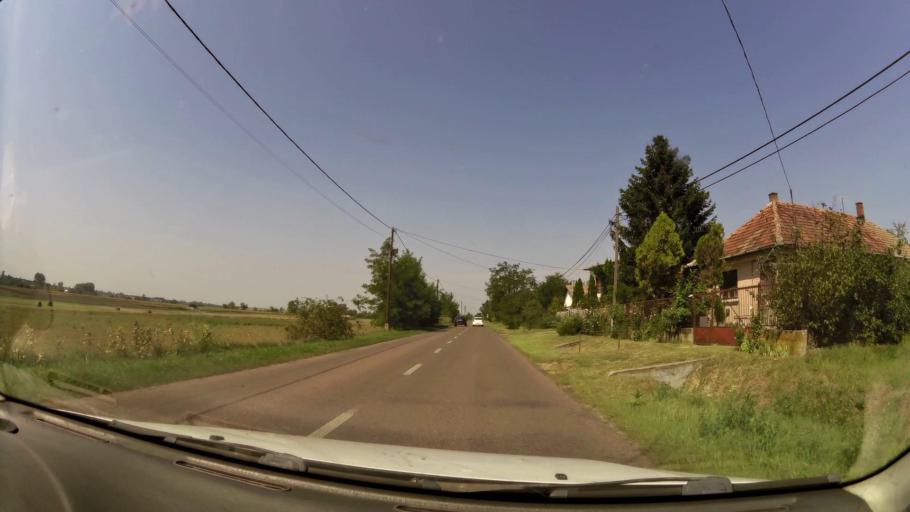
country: HU
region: Pest
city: Tapiobicske
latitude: 47.3717
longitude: 19.6763
